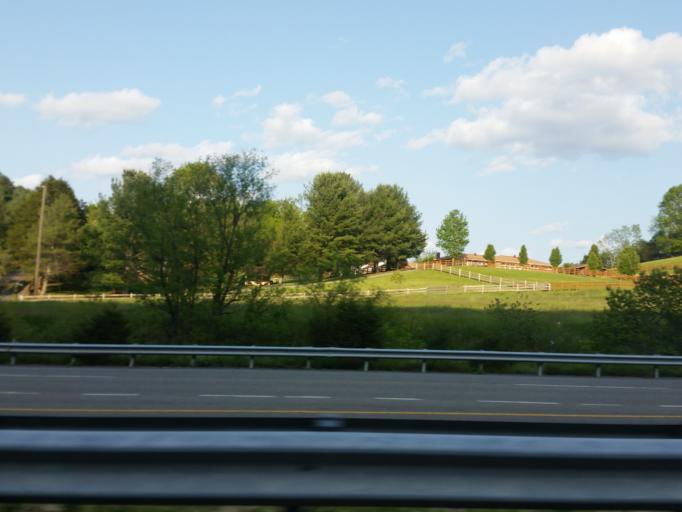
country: US
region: Virginia
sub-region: Tazewell County
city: Claypool Hill
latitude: 37.0210
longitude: -81.7972
